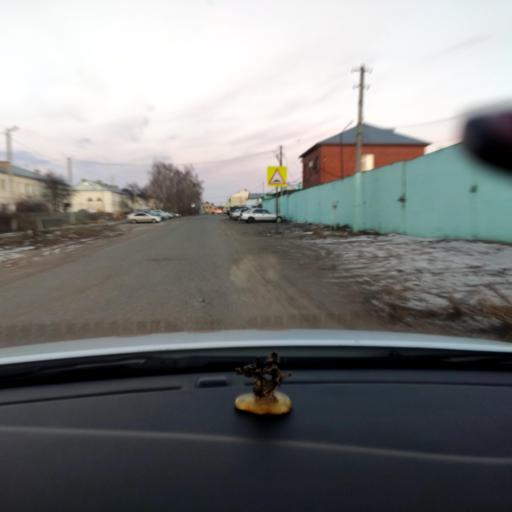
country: RU
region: Tatarstan
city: Stolbishchi
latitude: 55.6807
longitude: 49.2089
